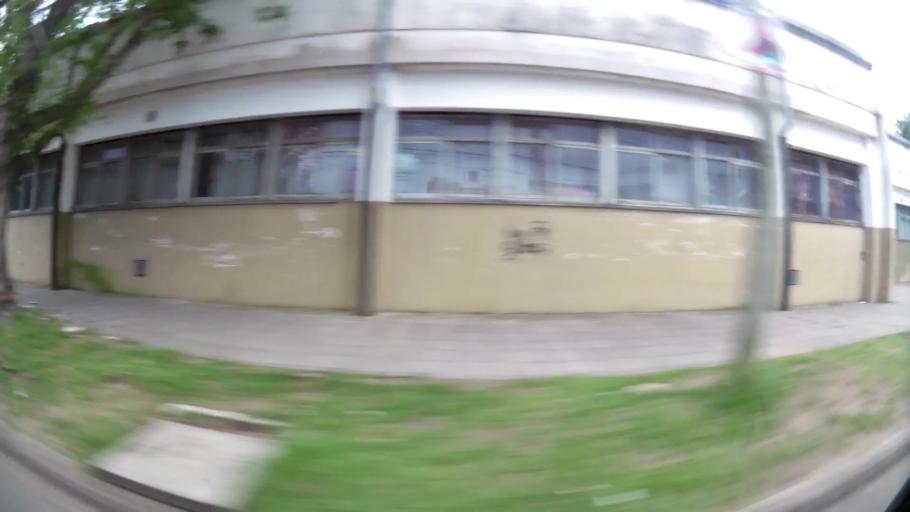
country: AR
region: Santa Fe
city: Granadero Baigorria
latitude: -32.8824
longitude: -60.7000
